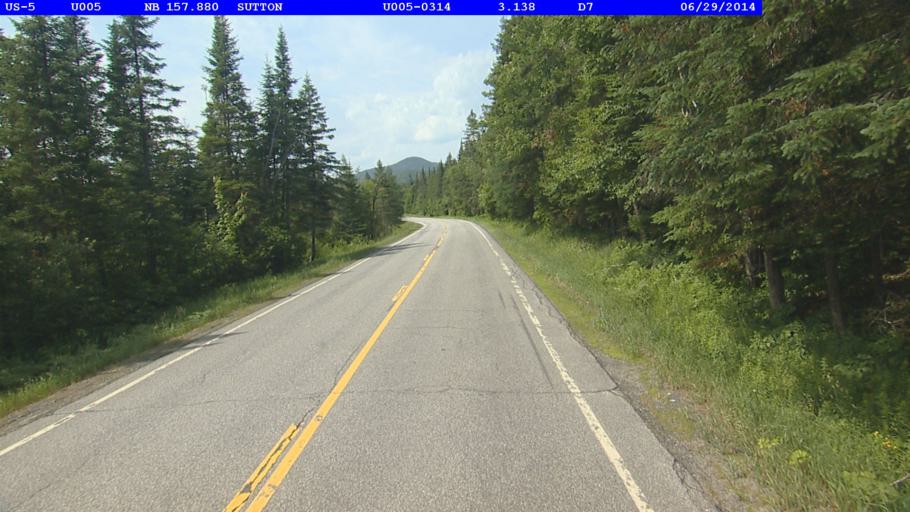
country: US
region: Vermont
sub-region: Caledonia County
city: Lyndonville
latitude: 44.6716
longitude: -72.0272
